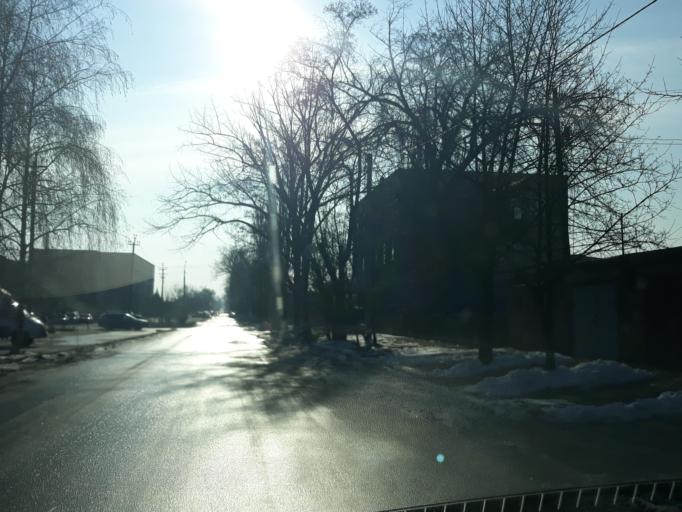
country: RU
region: Rostov
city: Taganrog
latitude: 47.2271
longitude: 38.9068
